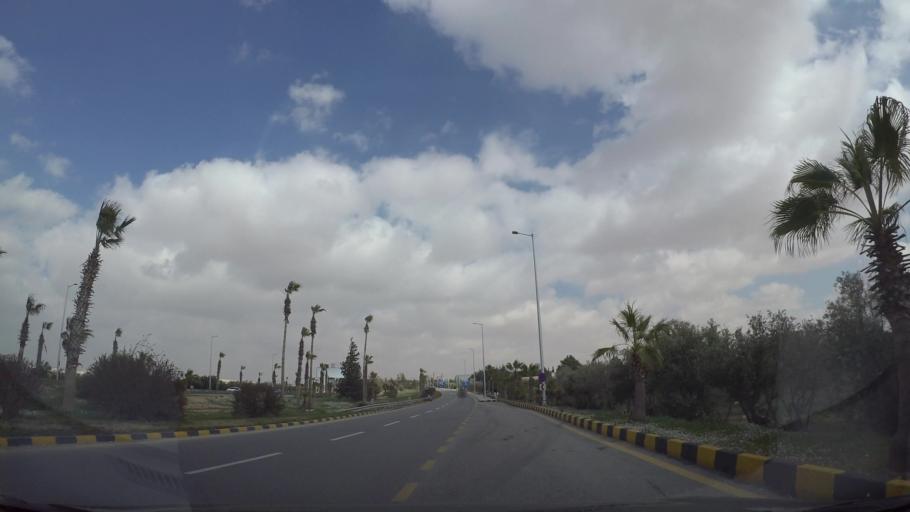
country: JO
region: Amman
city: Al Jizah
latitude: 31.7202
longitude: 35.9726
